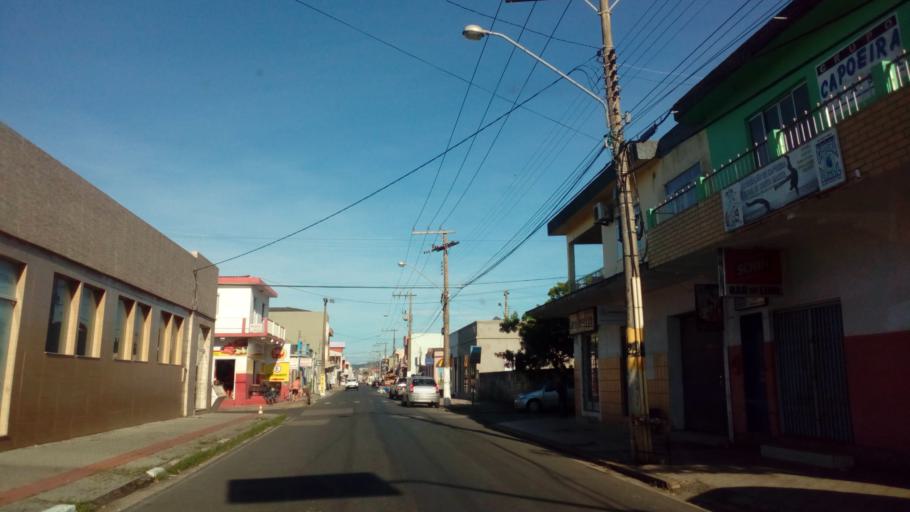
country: BR
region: Santa Catarina
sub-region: Laguna
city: Laguna
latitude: -28.4945
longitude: -48.7767
